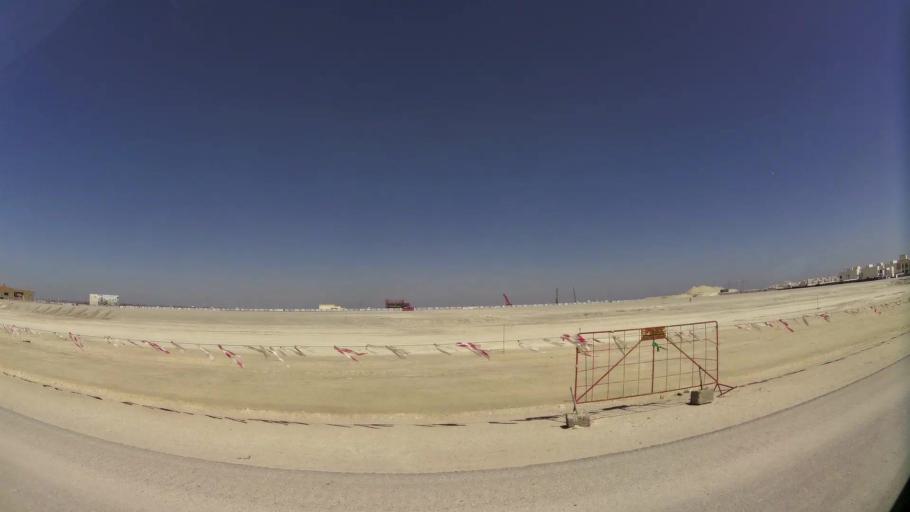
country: BH
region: Muharraq
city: Al Muharraq
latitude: 26.3018
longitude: 50.6295
